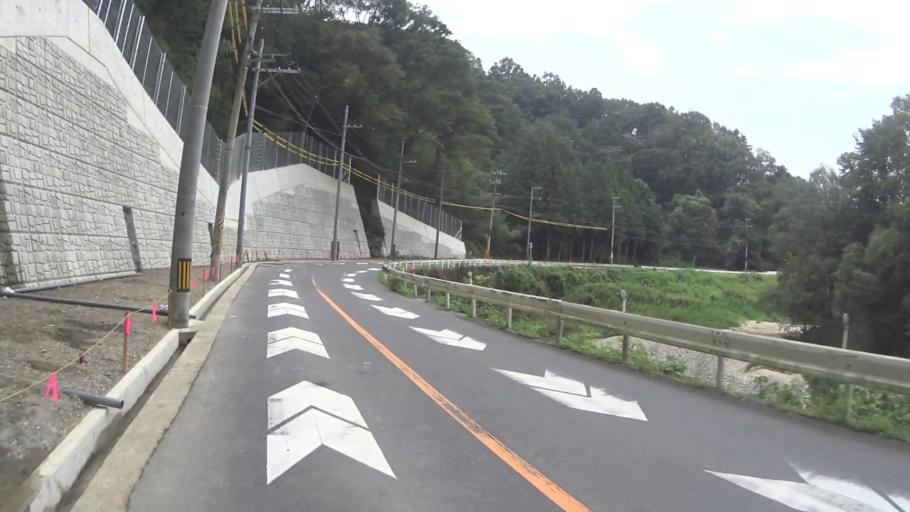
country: JP
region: Nara
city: Nara-shi
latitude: 34.7732
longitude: 135.8810
